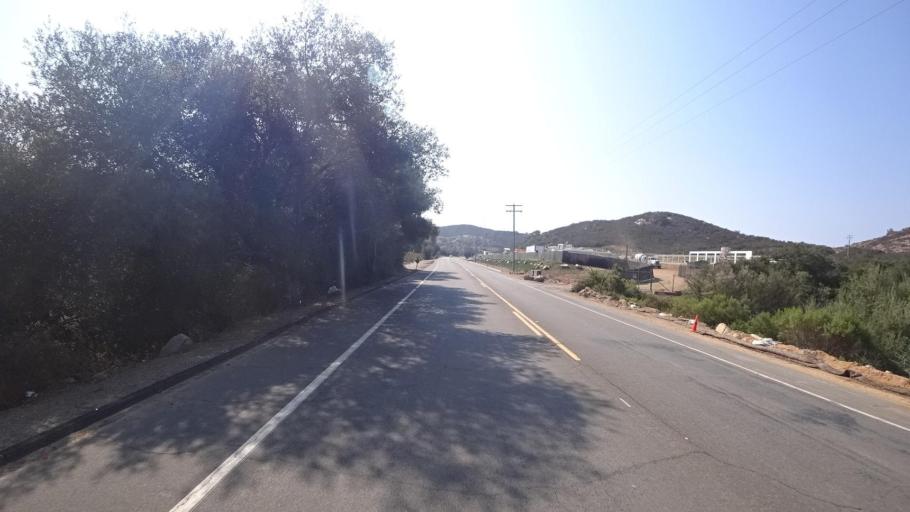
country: US
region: California
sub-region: San Diego County
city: Hidden Meadows
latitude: 33.1722
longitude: -117.1081
